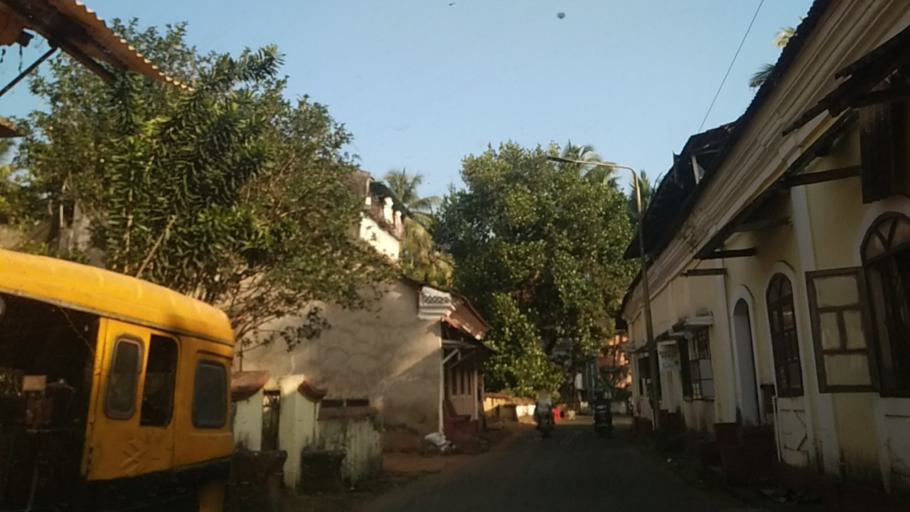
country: IN
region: Goa
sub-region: South Goa
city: Madgaon
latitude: 15.2802
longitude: 73.9561
